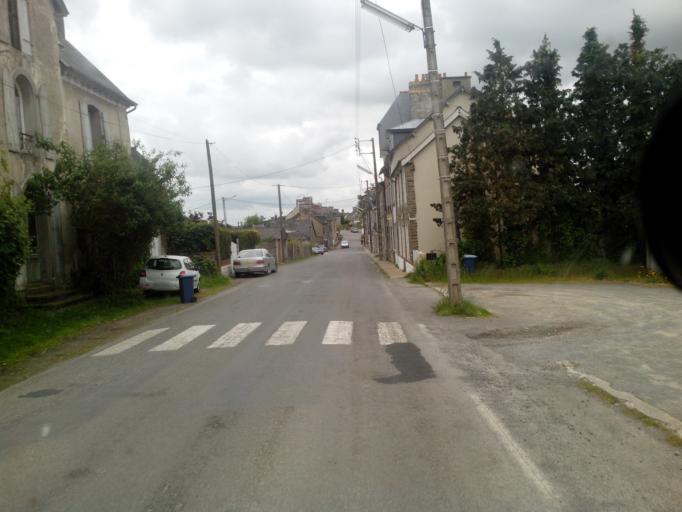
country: FR
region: Brittany
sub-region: Departement d'Ille-et-Vilaine
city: Saint-Medard-sur-Ille
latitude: 48.2488
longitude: -1.6562
